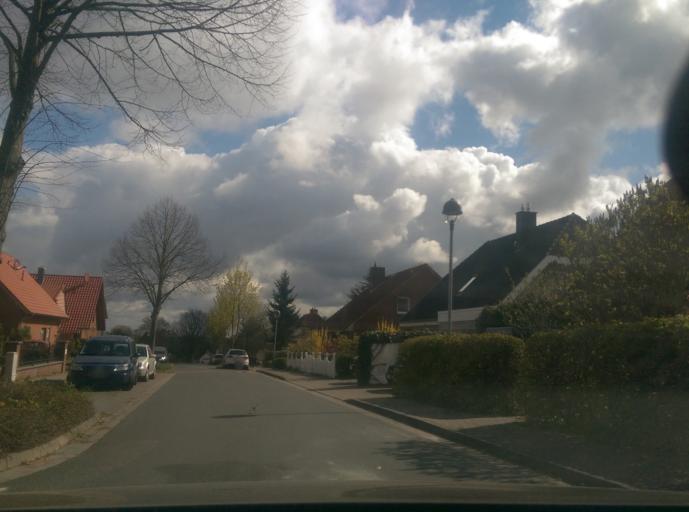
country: DE
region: Lower Saxony
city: Elze
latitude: 52.5417
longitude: 9.7233
